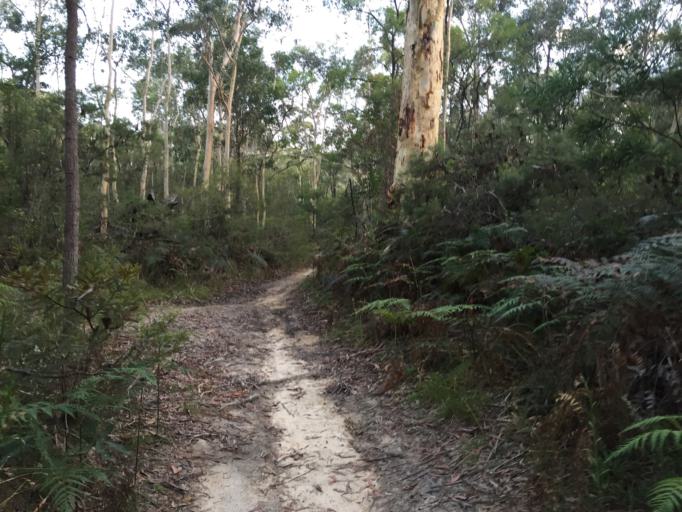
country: AU
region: New South Wales
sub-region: Blue Mountains Municipality
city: Blaxland
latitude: -33.7341
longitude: 150.6200
